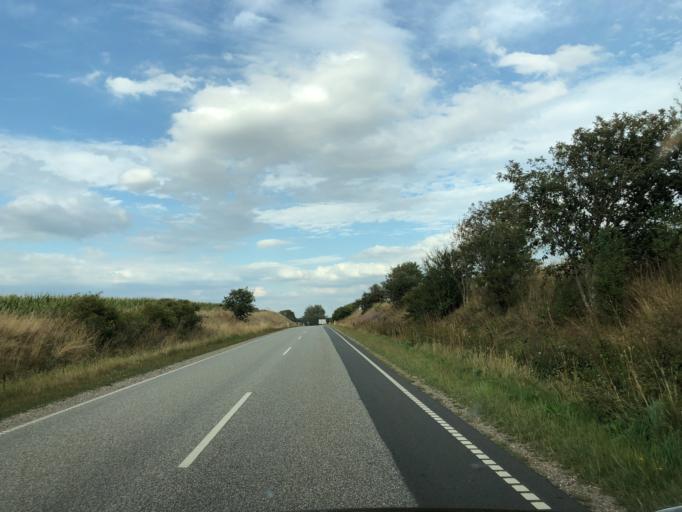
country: DK
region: Central Jutland
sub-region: Struer Kommune
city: Struer
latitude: 56.4122
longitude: 8.4814
